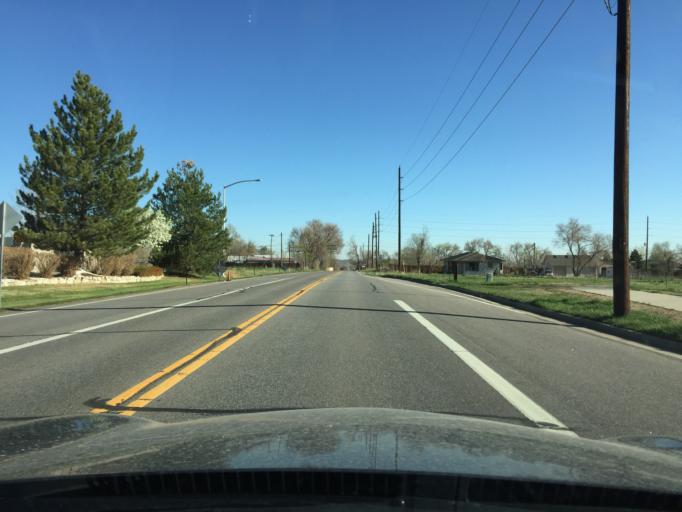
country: US
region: Colorado
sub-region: Boulder County
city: Erie
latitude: 40.0427
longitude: -105.0745
